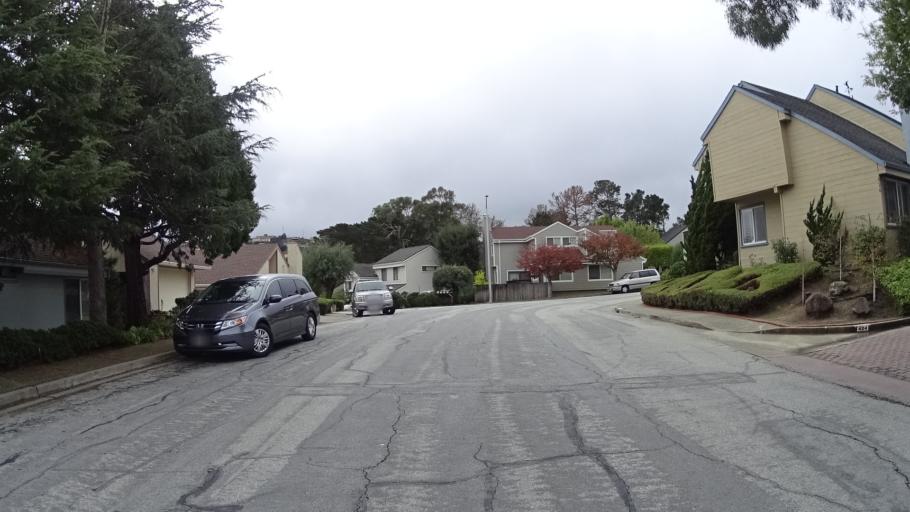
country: US
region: California
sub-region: San Mateo County
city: Millbrae
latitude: 37.6037
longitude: -122.4040
